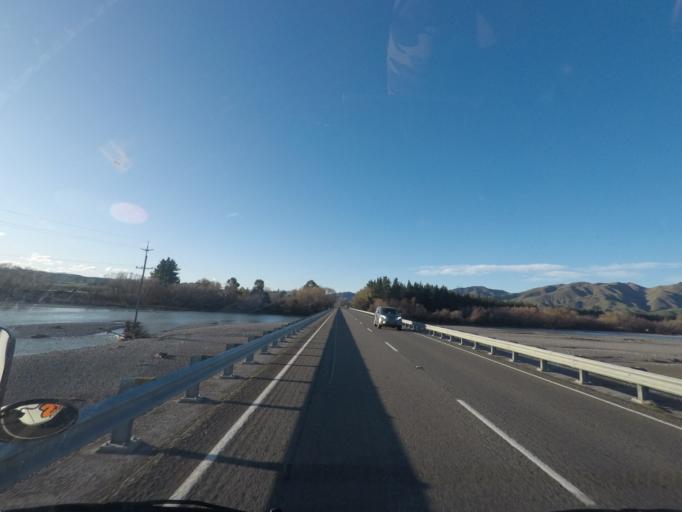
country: NZ
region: Canterbury
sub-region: Kaikoura District
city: Kaikoura
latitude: -42.7216
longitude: 173.2841
